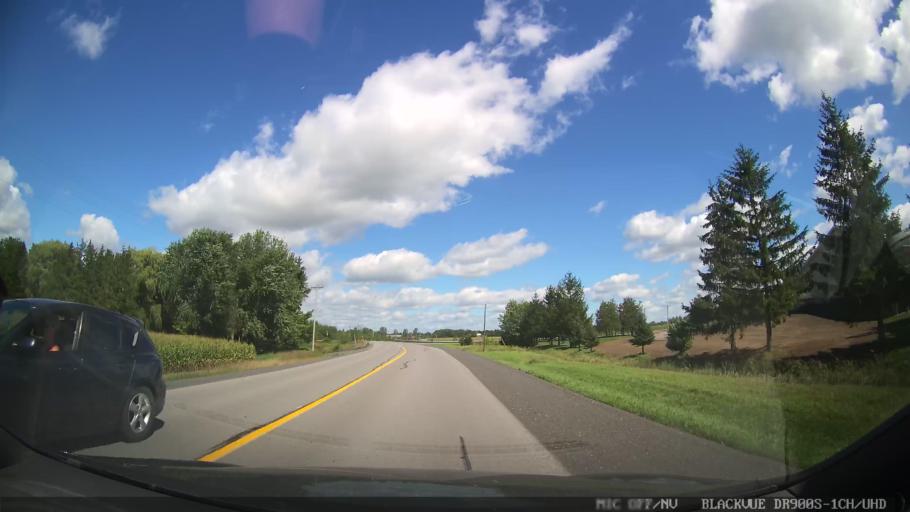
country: CA
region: Ontario
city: Bells Corners
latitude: 45.1825
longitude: -75.7490
